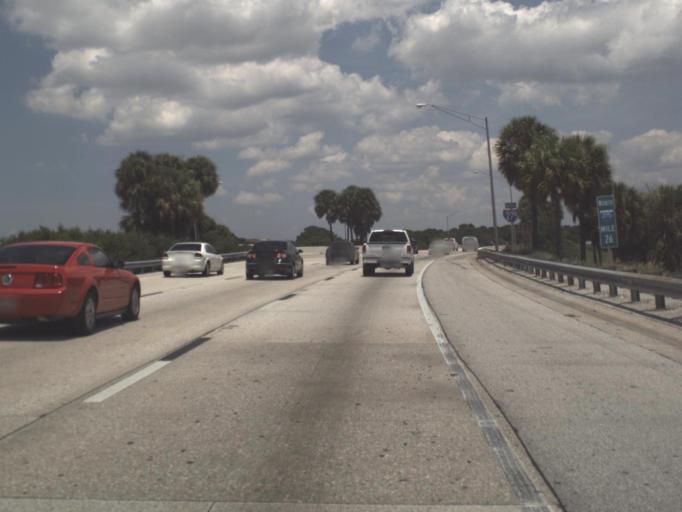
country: US
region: Florida
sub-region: Pinellas County
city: Lealman
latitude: 27.8274
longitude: -82.6663
